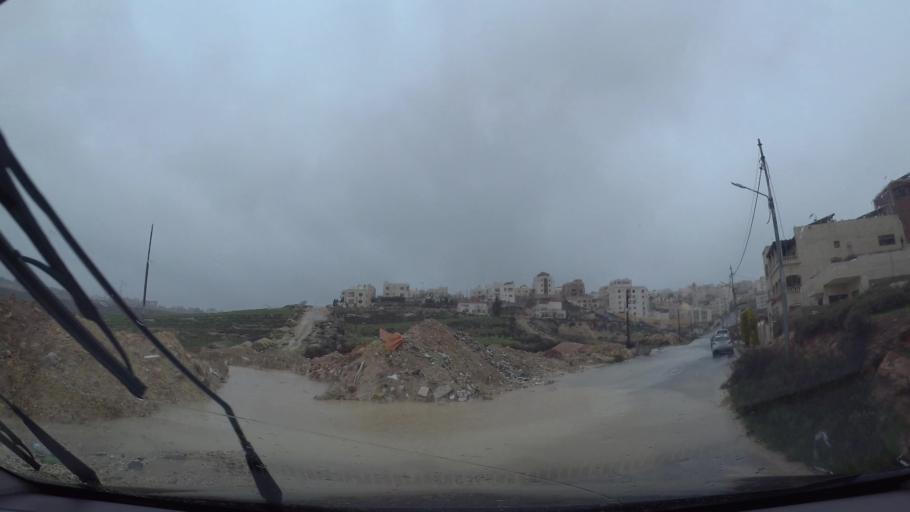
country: JO
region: Amman
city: Al Jubayhah
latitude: 32.0094
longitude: 35.9028
